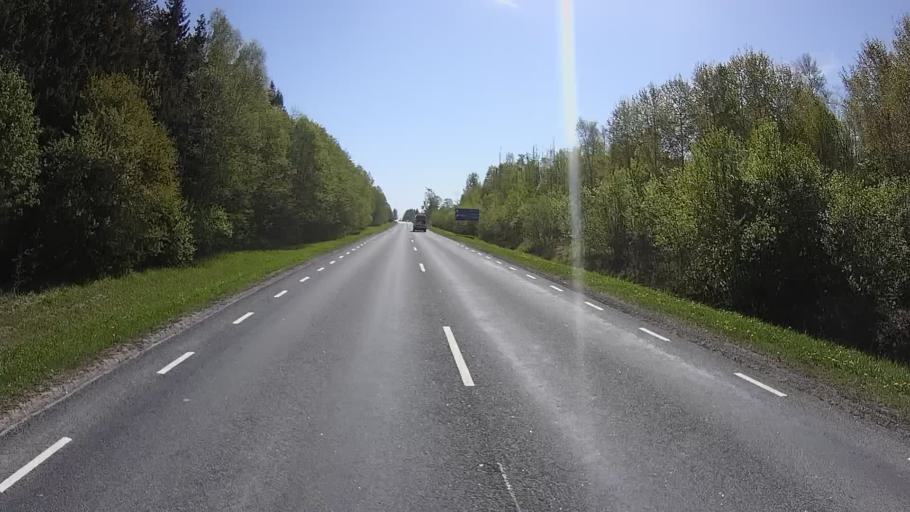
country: EE
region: Laeaene
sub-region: Lihula vald
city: Lihula
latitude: 58.5477
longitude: 23.9937
